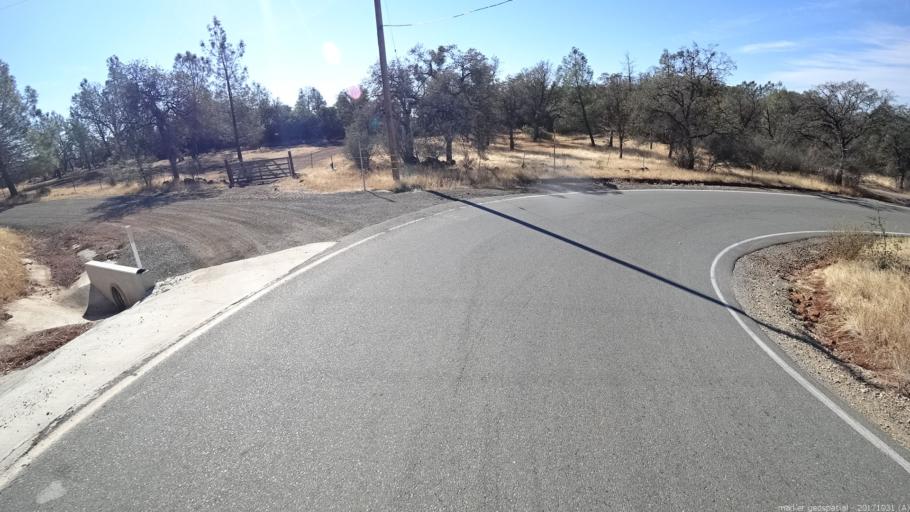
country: US
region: California
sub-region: Shasta County
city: Shingletown
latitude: 40.4649
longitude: -121.8821
